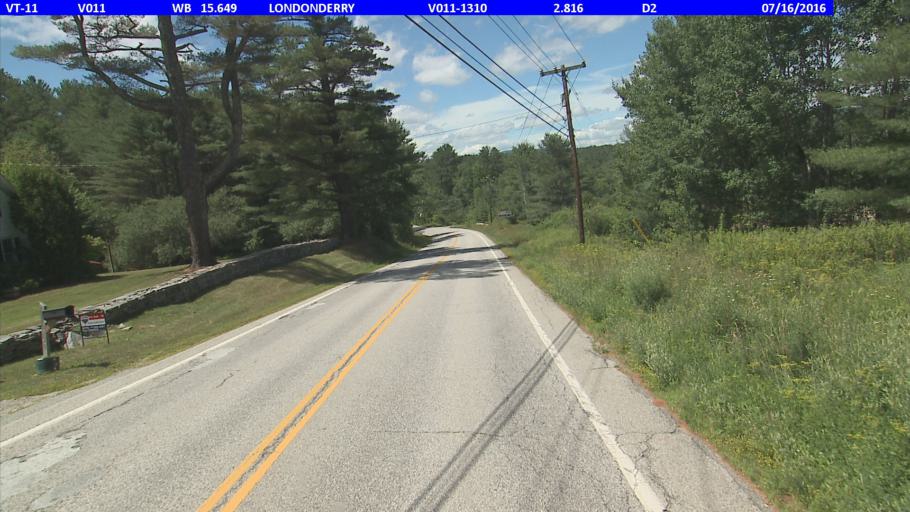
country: US
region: Vermont
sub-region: Windsor County
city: Chester
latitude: 43.2243
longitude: -72.7994
